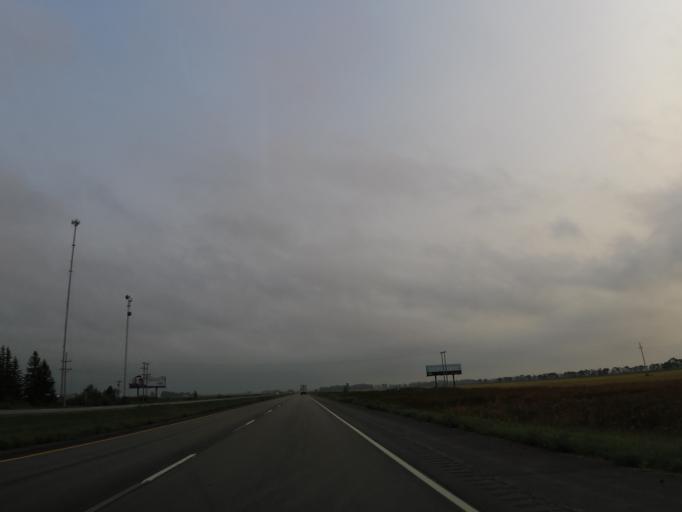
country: US
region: North Dakota
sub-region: Walsh County
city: Grafton
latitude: 48.5587
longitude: -97.1865
